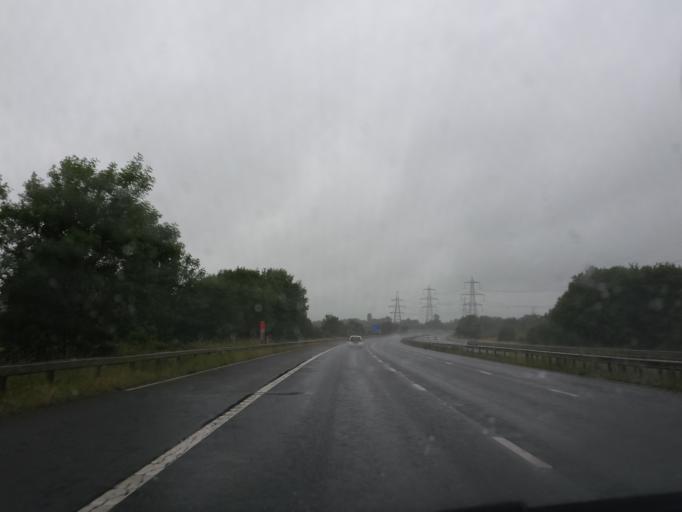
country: GB
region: England
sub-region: Leicestershire
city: Hinckley
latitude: 52.5270
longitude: -1.3302
